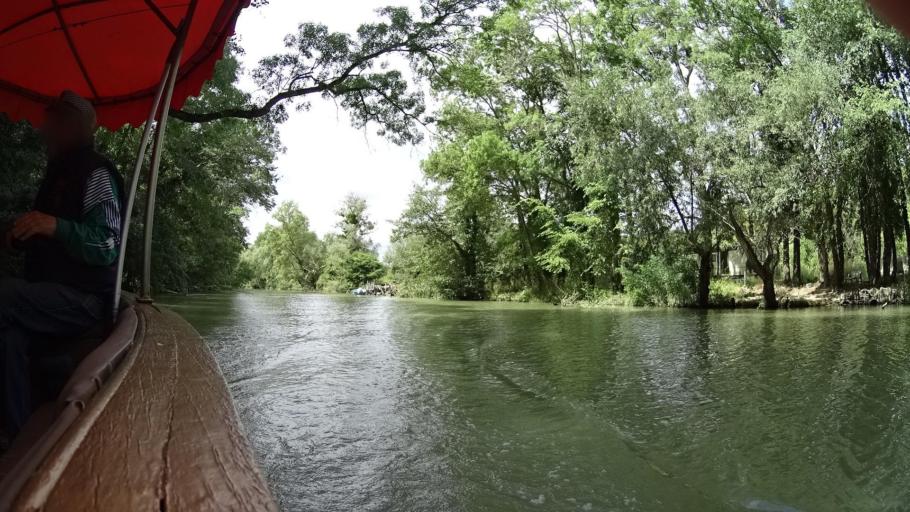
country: BG
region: Varna
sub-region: Obshtina Byala
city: Byala
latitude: 43.0234
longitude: 27.8731
